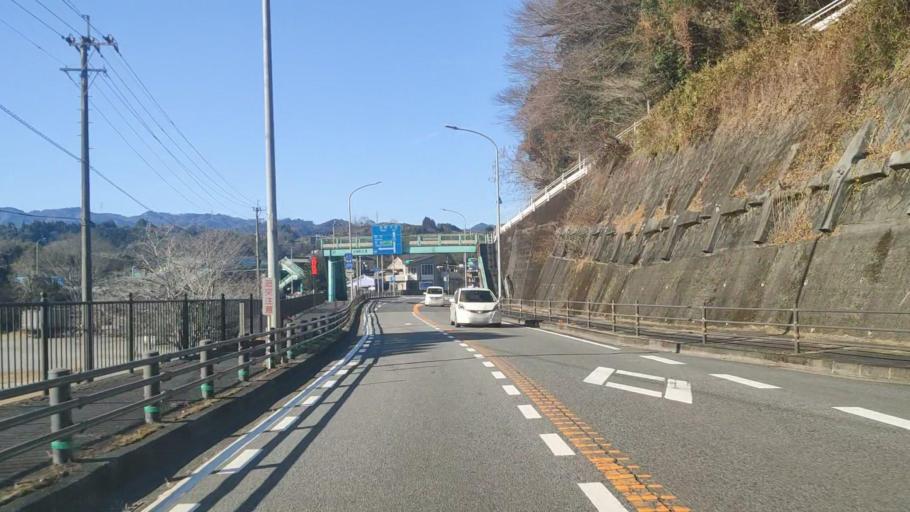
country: JP
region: Oita
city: Oita
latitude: 33.0711
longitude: 131.6393
